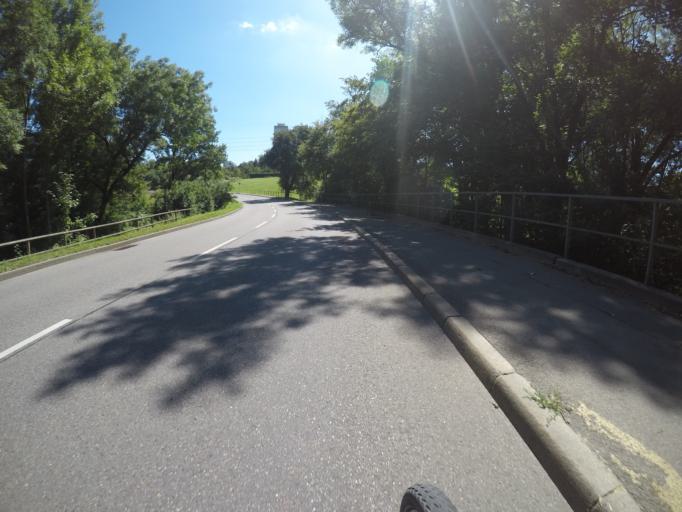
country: DE
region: Baden-Wuerttemberg
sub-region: Regierungsbezirk Stuttgart
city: Leinfelden-Echterdingen
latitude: 48.7170
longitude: 9.1613
